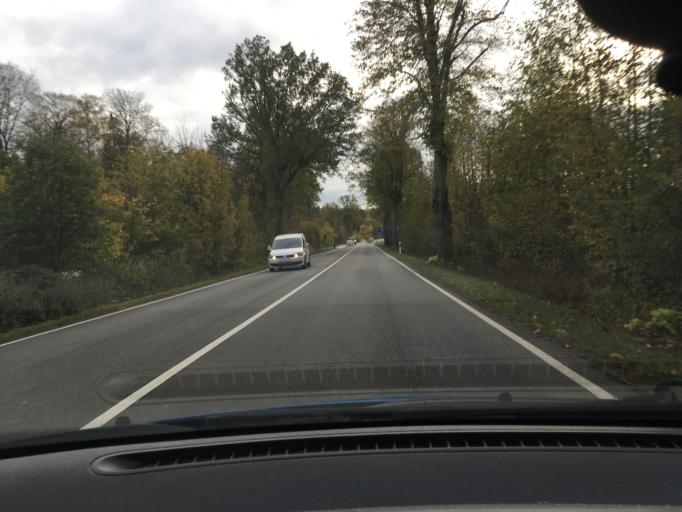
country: DE
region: Schleswig-Holstein
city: Talkau
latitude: 53.5672
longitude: 10.5636
